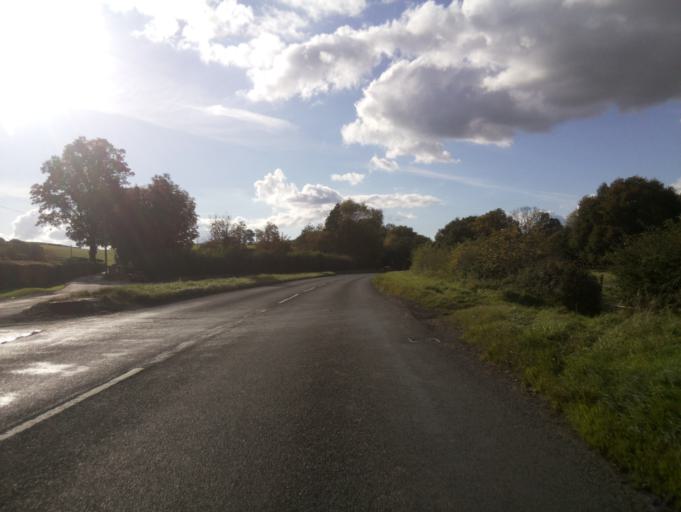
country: GB
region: Wales
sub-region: Sir Powys
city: Hay
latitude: 52.0491
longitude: -3.1834
